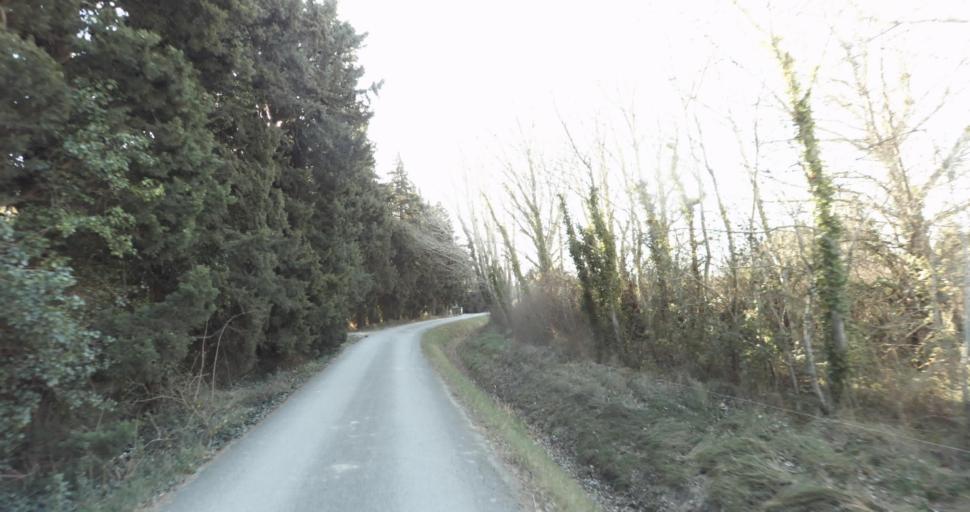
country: FR
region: Provence-Alpes-Cote d'Azur
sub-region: Departement des Bouches-du-Rhone
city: Rognonas
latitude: 43.9124
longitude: 4.7798
